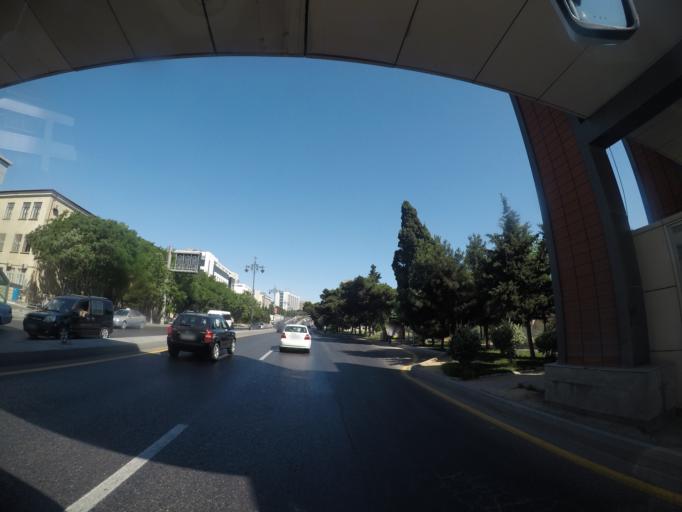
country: AZ
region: Baki
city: Khodzhi-Gasan
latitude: 40.3985
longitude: 49.8127
